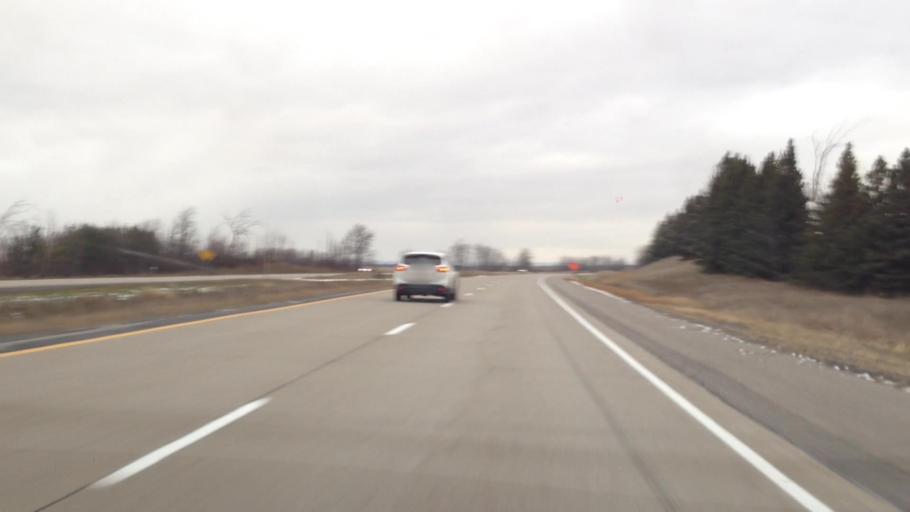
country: CA
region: Ontario
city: Hawkesbury
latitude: 45.4103
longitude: -74.7704
